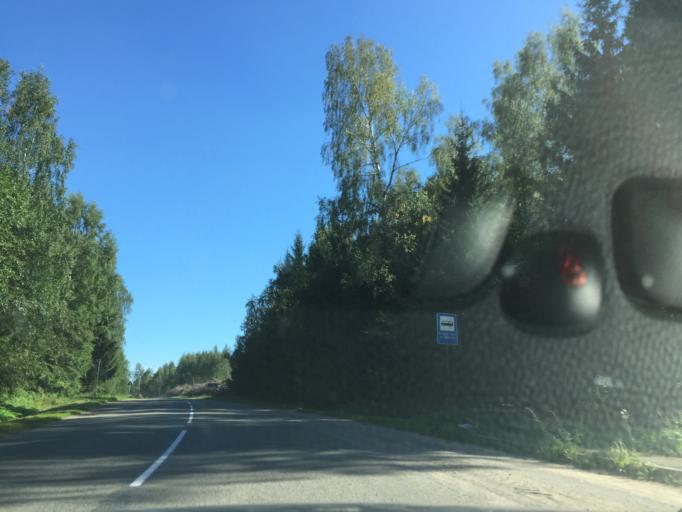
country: LV
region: Akniste
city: Akniste
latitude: 56.1138
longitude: 25.8381
